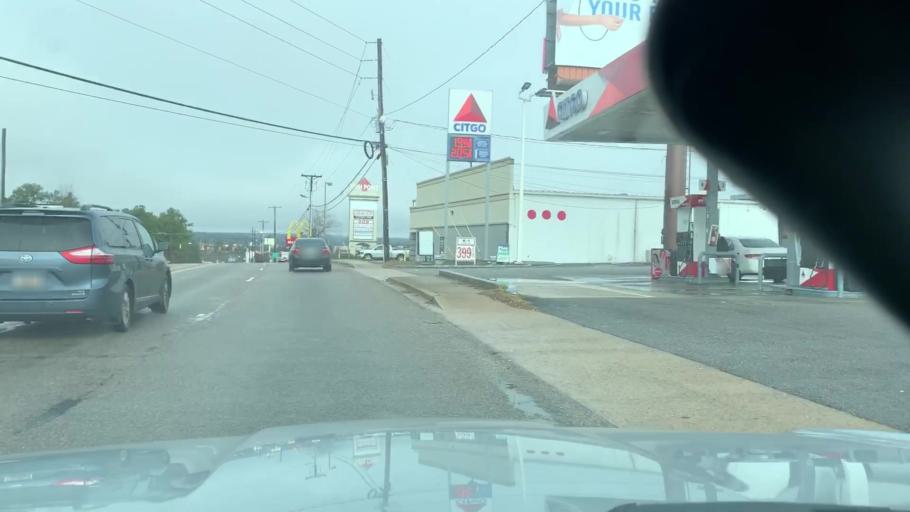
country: US
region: South Carolina
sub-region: Richland County
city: Woodfield
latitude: 34.0520
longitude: -80.9453
